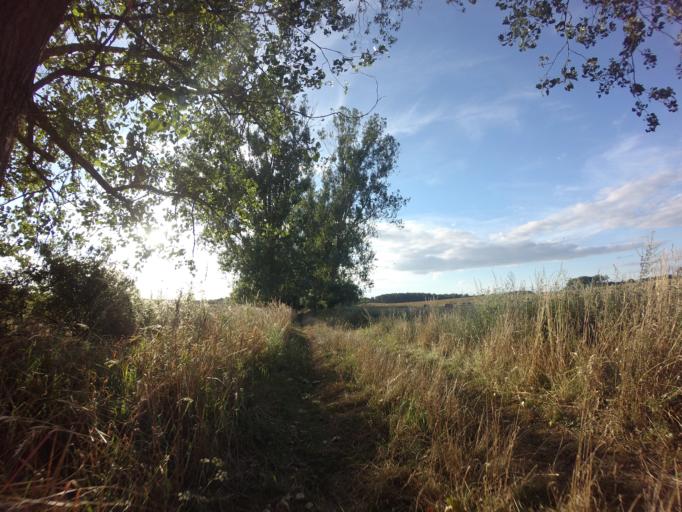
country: PL
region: West Pomeranian Voivodeship
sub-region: Powiat choszczenski
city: Choszczno
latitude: 53.1179
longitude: 15.4248
